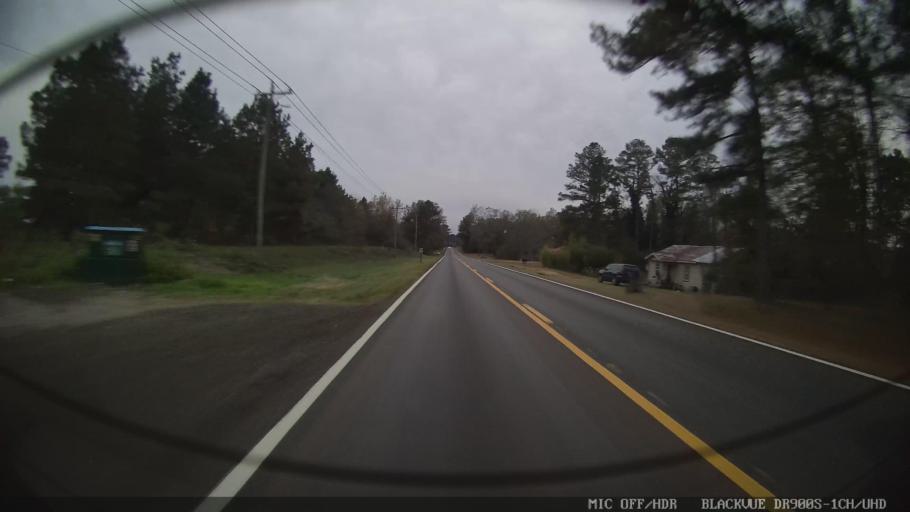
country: US
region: Mississippi
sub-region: Clarke County
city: Quitman
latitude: 32.0509
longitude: -88.6910
